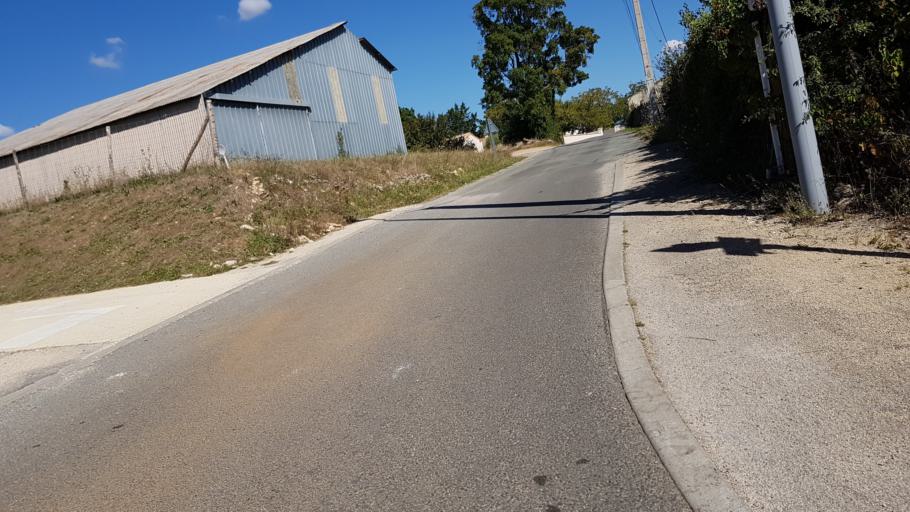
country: FR
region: Poitou-Charentes
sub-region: Departement des Deux-Sevres
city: Vouille
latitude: 46.3208
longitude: -0.3704
